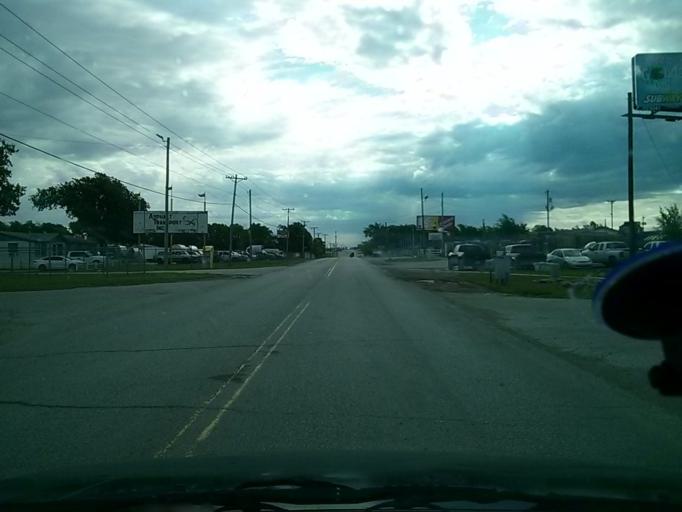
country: US
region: Oklahoma
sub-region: Rogers County
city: Catoosa
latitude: 36.1606
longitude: -95.8408
